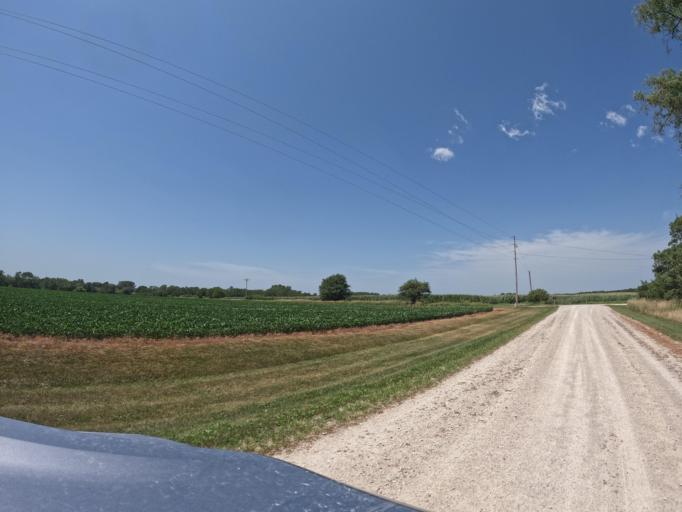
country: US
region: Iowa
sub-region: Henry County
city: Mount Pleasant
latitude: 40.9444
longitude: -91.6462
